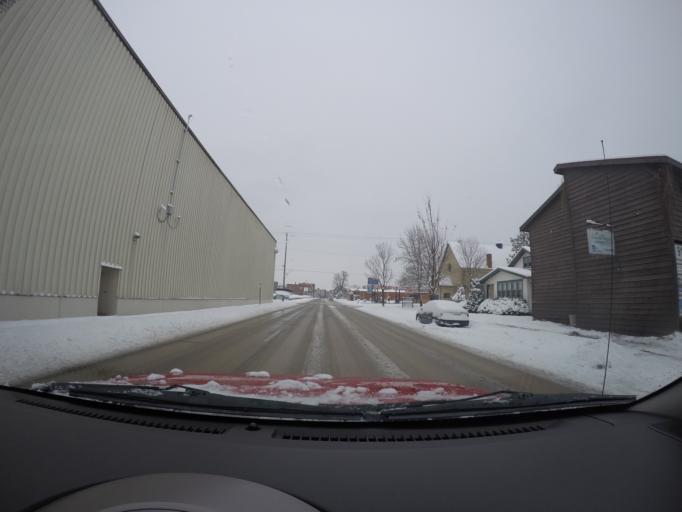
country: US
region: Wisconsin
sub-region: La Crosse County
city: La Crosse
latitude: 43.8040
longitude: -91.2519
